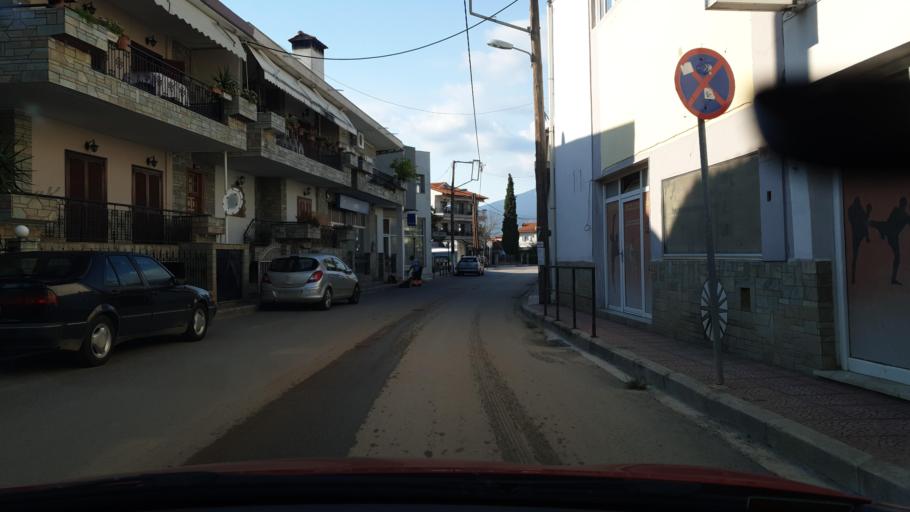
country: GR
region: Central Macedonia
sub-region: Nomos Thessalonikis
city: Vasilika
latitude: 40.4814
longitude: 23.1366
